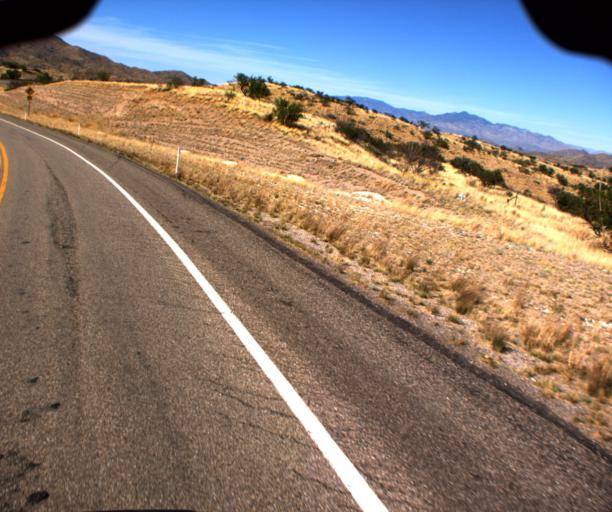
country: US
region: Arizona
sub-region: Pima County
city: Corona de Tucson
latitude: 31.8271
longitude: -110.7133
